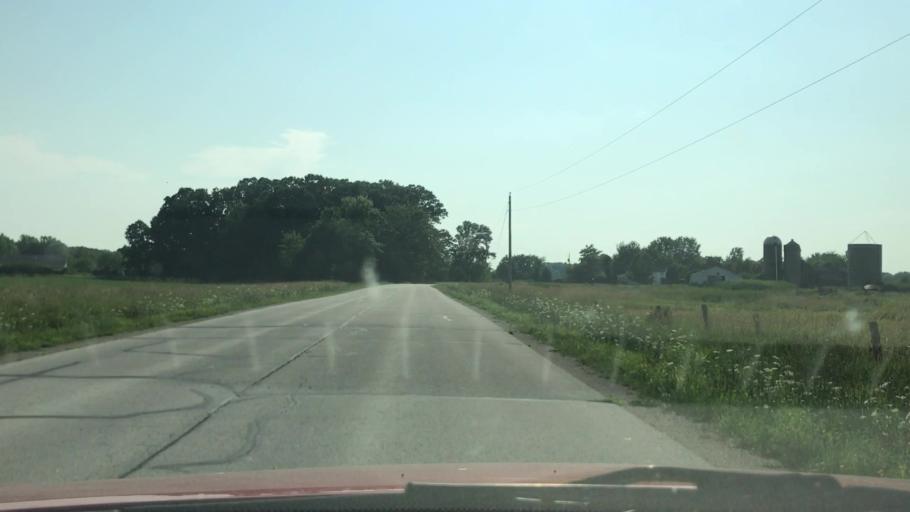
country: US
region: Wisconsin
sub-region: Brown County
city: Oneida
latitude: 44.4303
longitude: -88.1535
